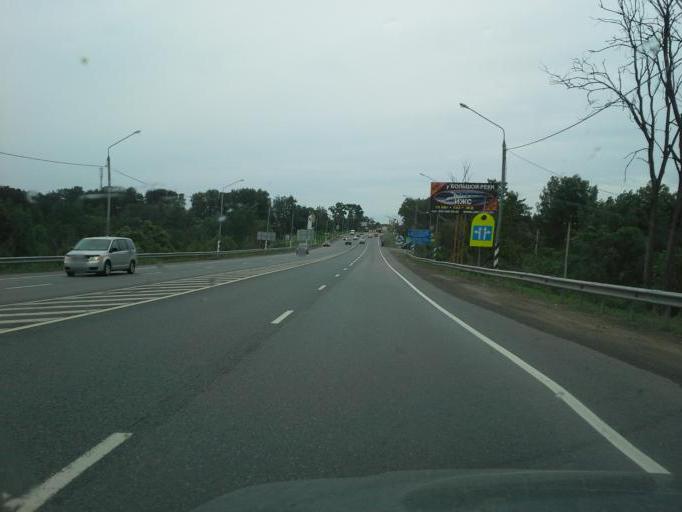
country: RU
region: Moskovskaya
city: Malaya Dubna
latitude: 55.8992
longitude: 39.0577
